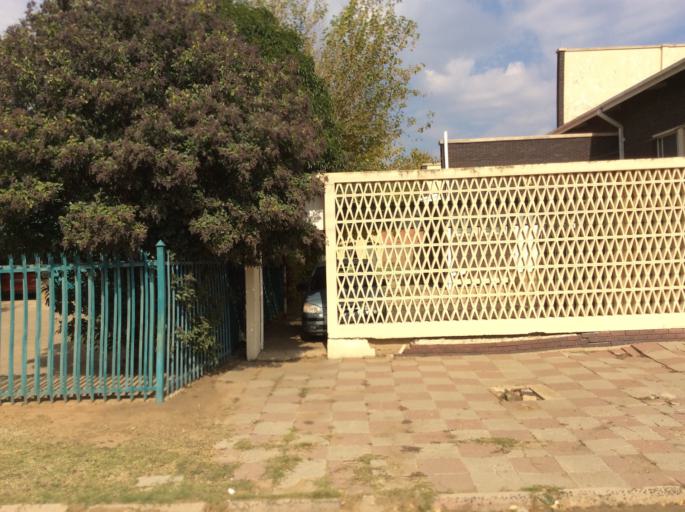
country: LS
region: Mafeteng
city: Mafeteng
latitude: -29.7295
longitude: 27.0392
